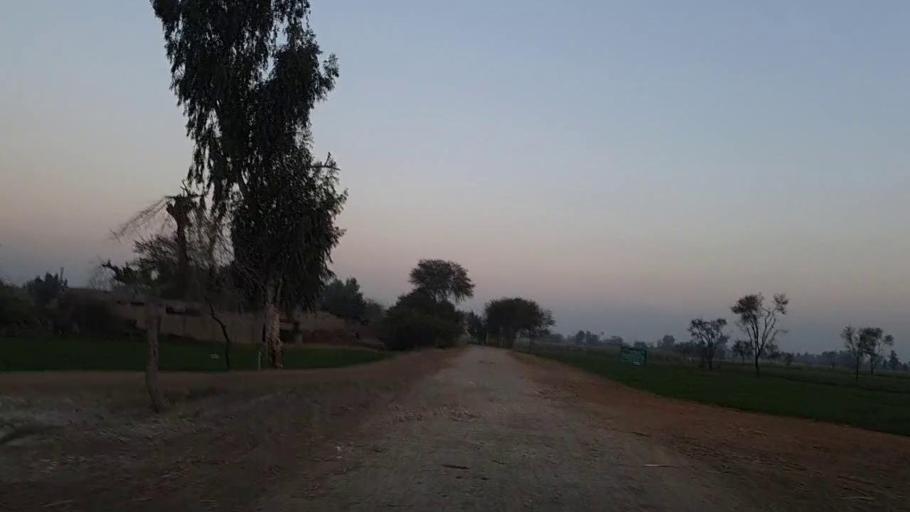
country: PK
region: Sindh
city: Naushahro Firoz
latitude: 26.7910
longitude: 68.0427
